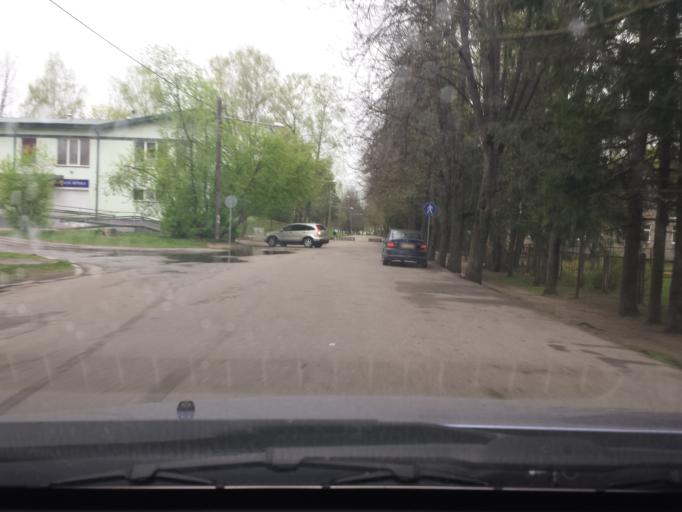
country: LV
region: Marupe
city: Marupe
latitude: 56.9609
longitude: 24.0289
